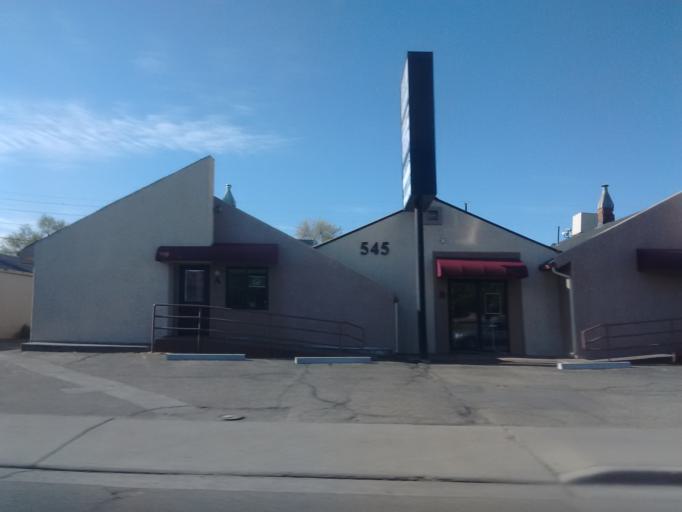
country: US
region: Colorado
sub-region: Mesa County
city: Grand Junction
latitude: 39.0774
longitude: -108.5635
